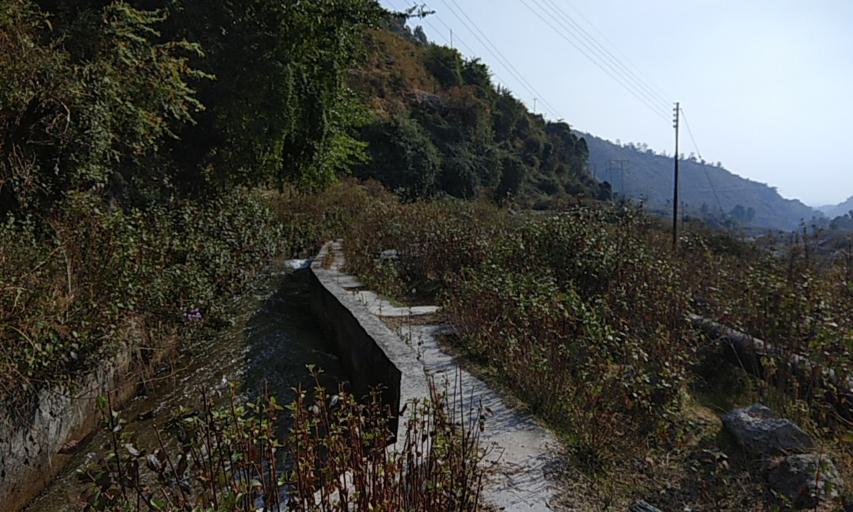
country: IN
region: Himachal Pradesh
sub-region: Kangra
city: Palampur
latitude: 32.1550
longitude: 76.5440
